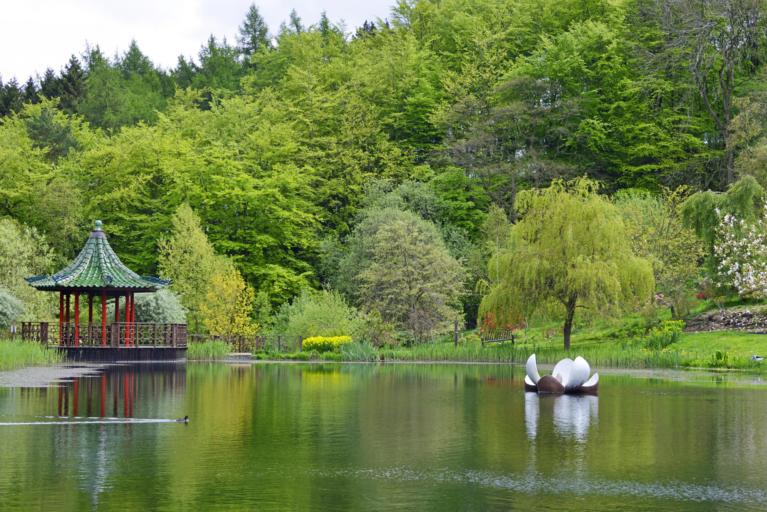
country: GB
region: England
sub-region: North Yorkshire
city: Bedale
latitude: 54.1914
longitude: -1.6727
